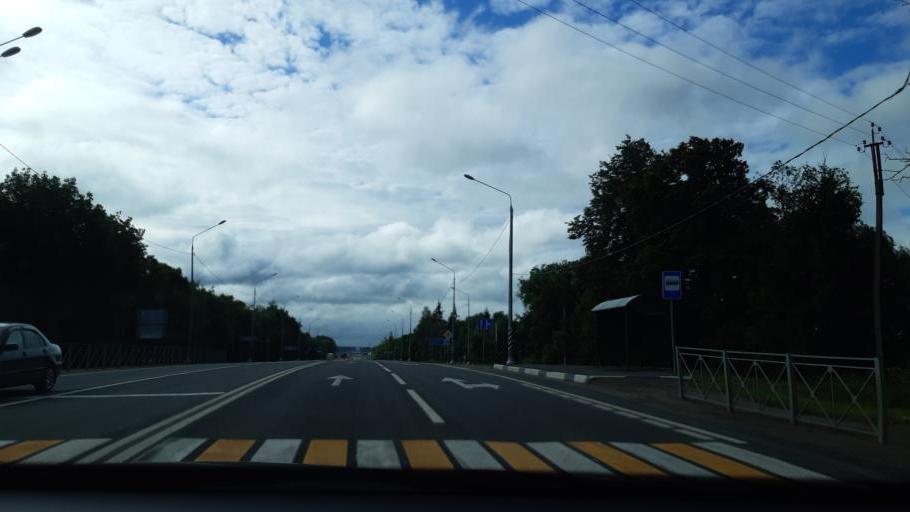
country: RU
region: Smolensk
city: Smolensk
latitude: 54.7166
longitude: 32.1076
